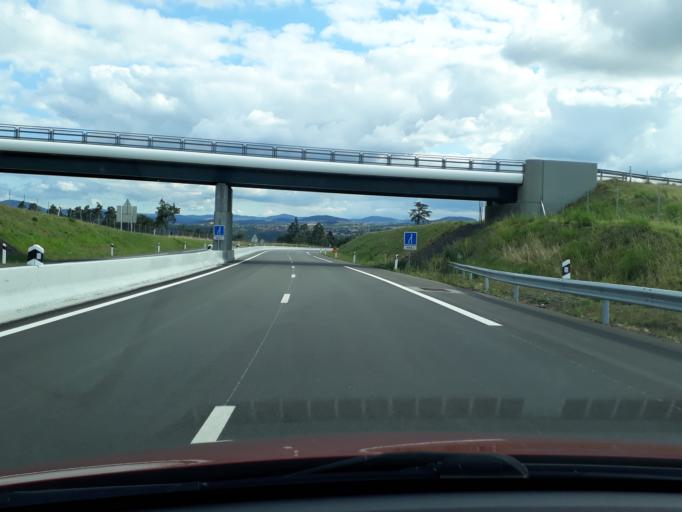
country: FR
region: Auvergne
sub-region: Departement de la Haute-Loire
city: Cussac-sur-Loire
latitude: 45.0088
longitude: 3.8831
